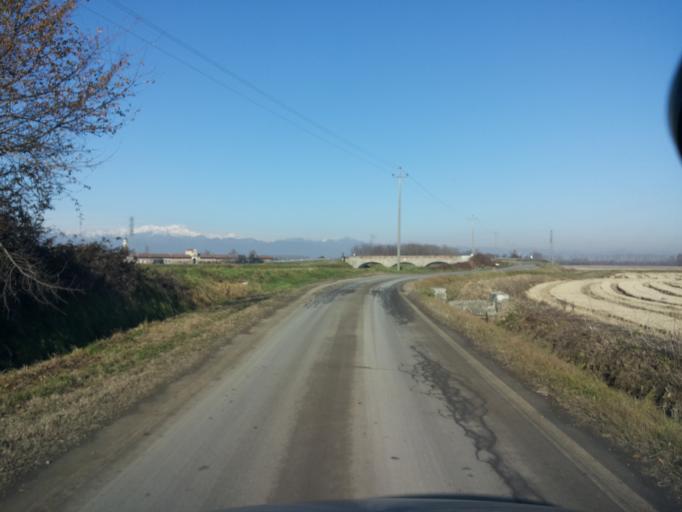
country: IT
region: Piedmont
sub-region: Provincia di Vercelli
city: San Germano Vercellese
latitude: 45.3883
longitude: 8.2439
